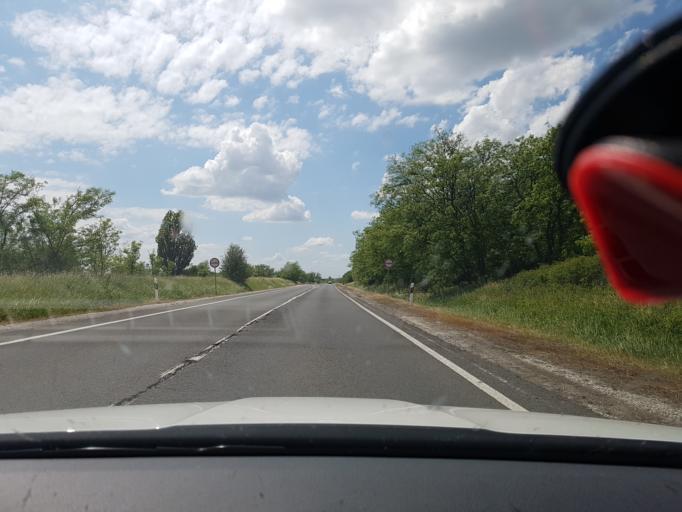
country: HU
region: Heves
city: Kompolt
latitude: 47.7534
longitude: 20.1731
